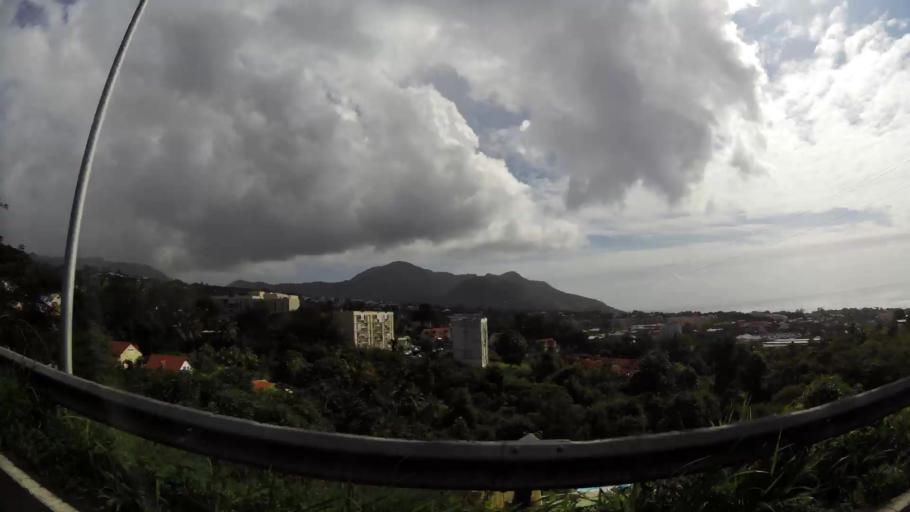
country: GP
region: Guadeloupe
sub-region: Guadeloupe
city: Basse-Terre
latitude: 16.0059
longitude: -61.7184
